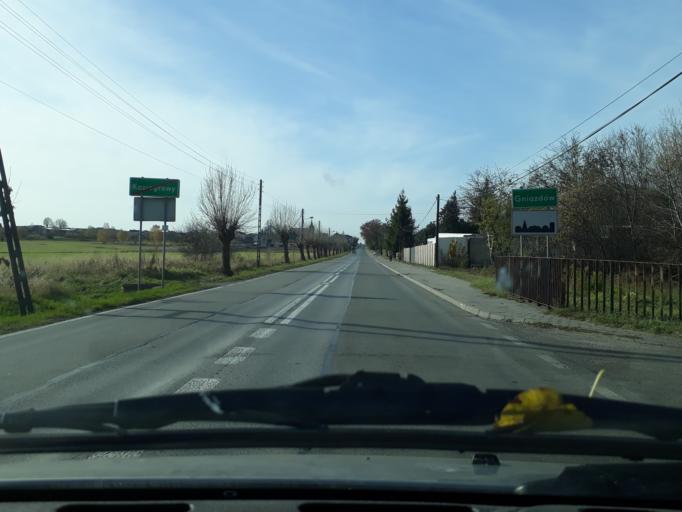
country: PL
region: Silesian Voivodeship
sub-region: Powiat myszkowski
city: Gniazdow
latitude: 50.5985
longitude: 19.1267
